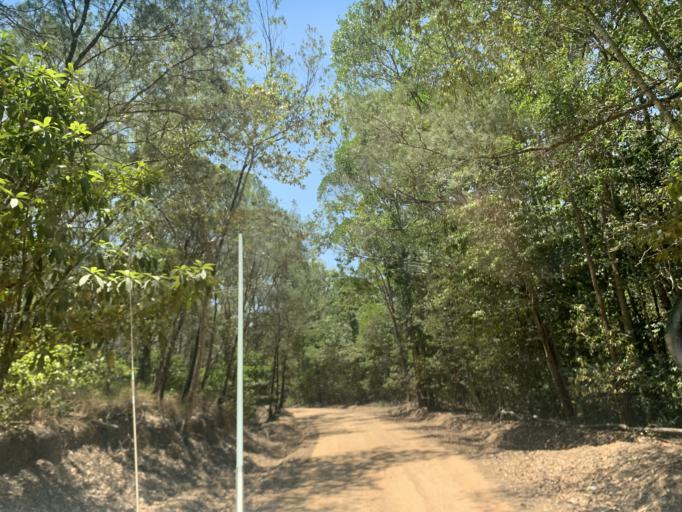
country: AU
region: Queensland
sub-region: Cairns
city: Redlynch
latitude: -16.9245
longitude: 145.6039
